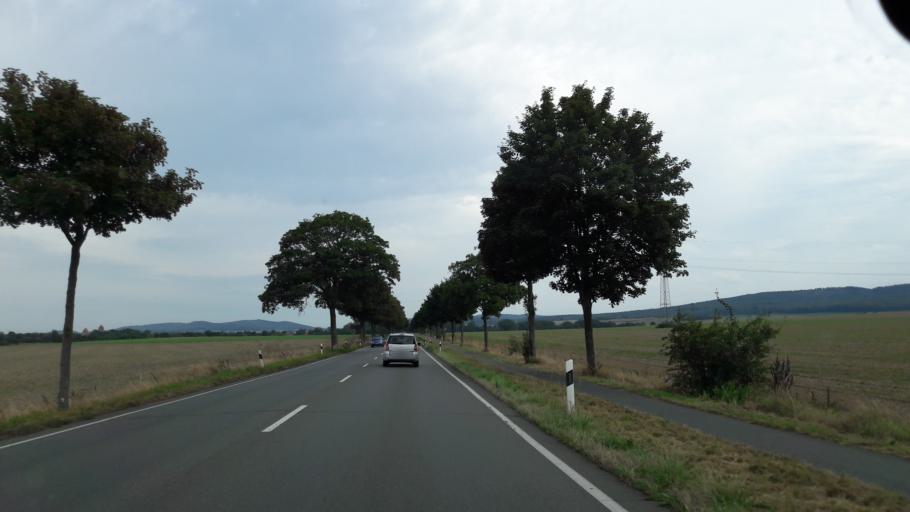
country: DE
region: Lower Saxony
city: Hildesheim
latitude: 52.1201
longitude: 9.9614
